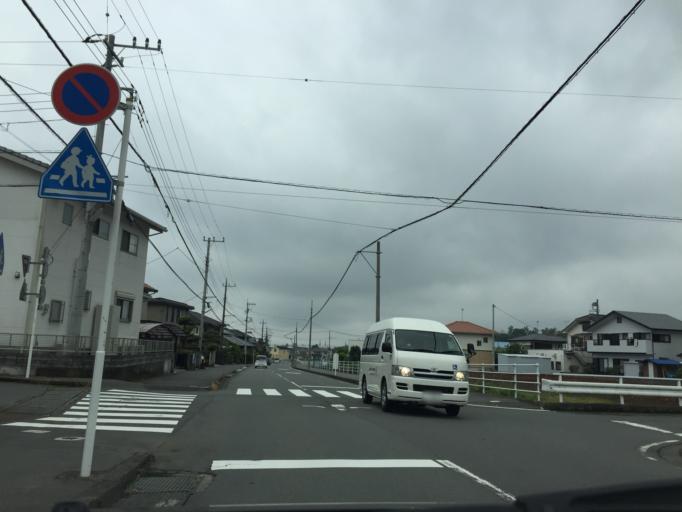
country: JP
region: Shizuoka
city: Mishima
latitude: 35.1750
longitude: 138.9251
